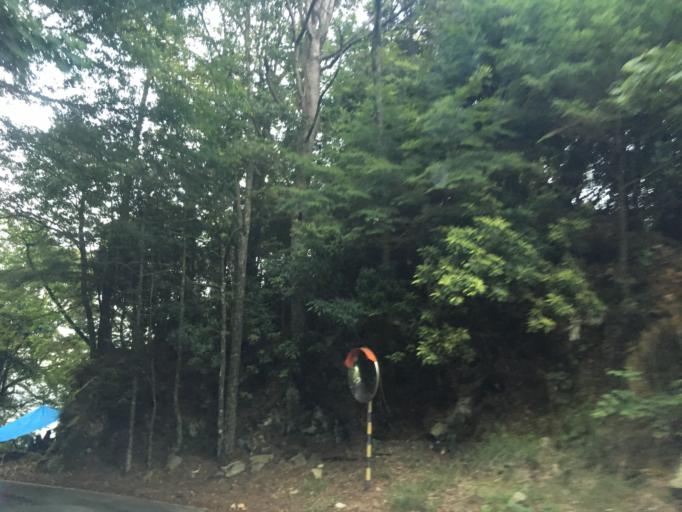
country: TW
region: Taiwan
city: Fengyuan
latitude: 24.2400
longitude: 120.9797
